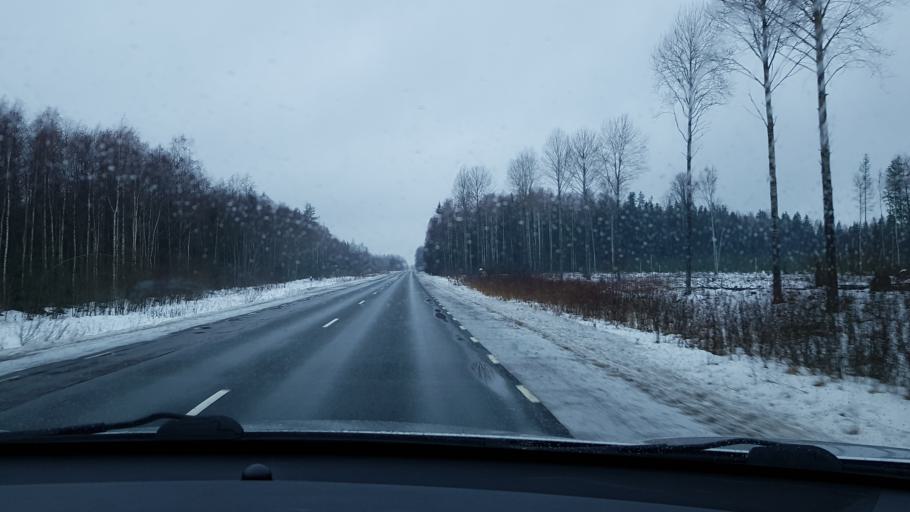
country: EE
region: Jaervamaa
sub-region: Tueri vald
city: Sarevere
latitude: 58.8011
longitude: 25.2333
